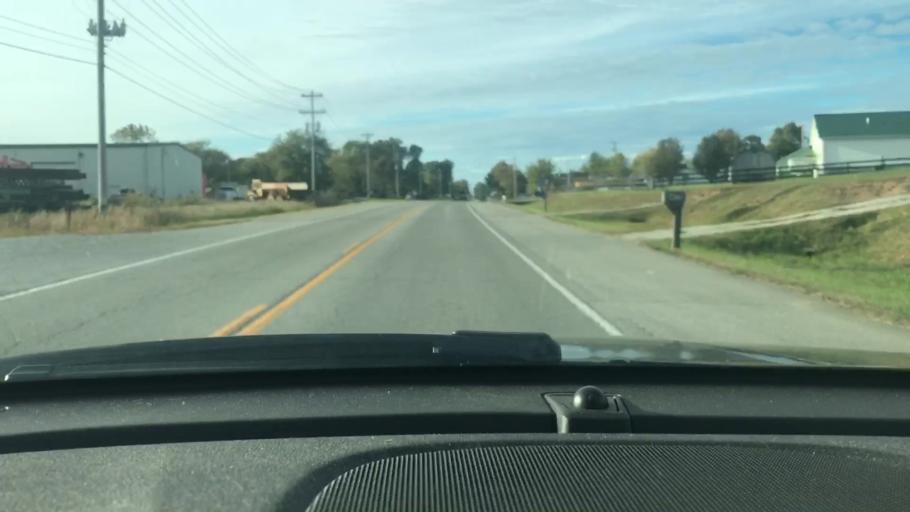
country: US
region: Tennessee
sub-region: Dickson County
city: White Bluff
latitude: 36.1335
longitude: -87.2352
